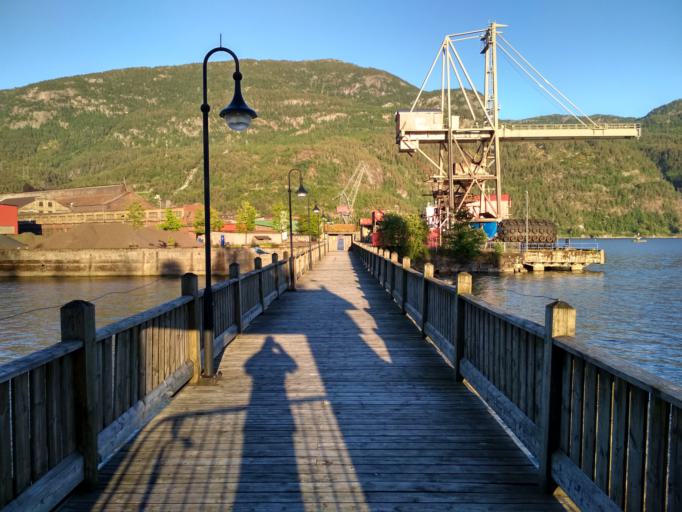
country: NO
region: Rogaland
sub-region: Sauda
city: Sauda
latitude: 59.6473
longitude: 6.3533
